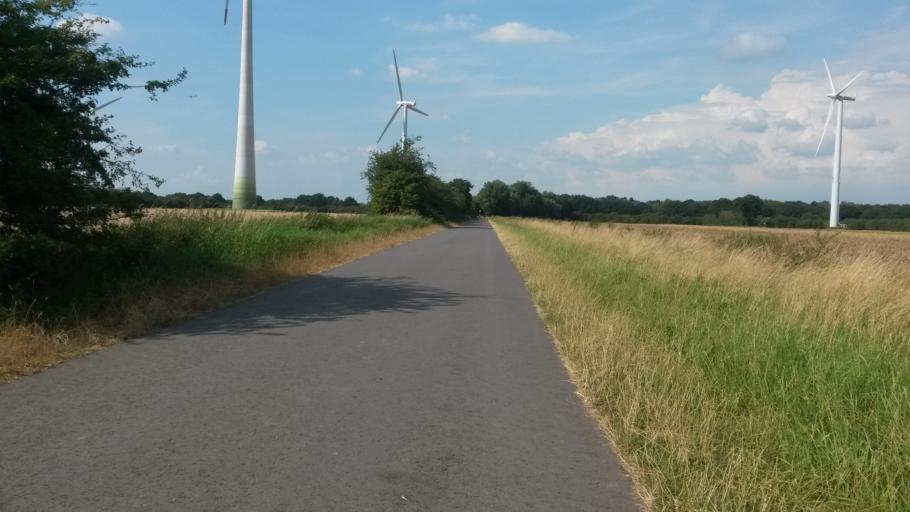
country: DE
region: Lower Saxony
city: Riede
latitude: 53.0229
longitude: 8.9306
